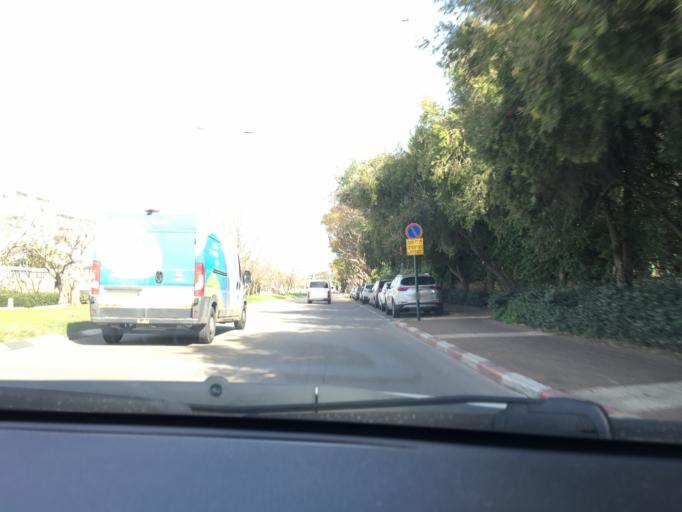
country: IL
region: Central District
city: Kfar Saba
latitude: 32.1846
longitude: 34.9016
